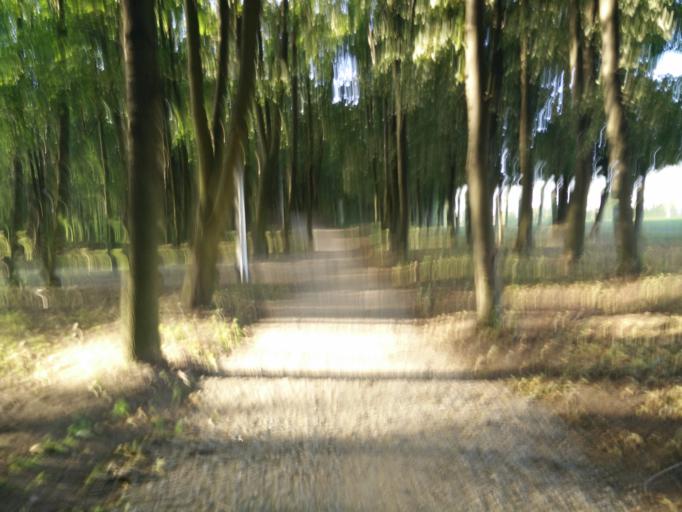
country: PL
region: Greater Poland Voivodeship
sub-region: Powiat sredzki
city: Sroda Wielkopolska
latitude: 52.2381
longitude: 17.2938
